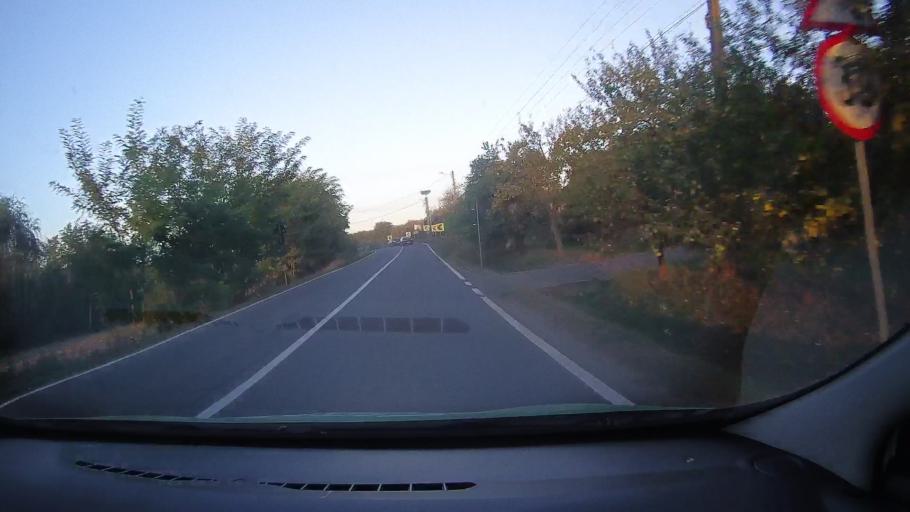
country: RO
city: Szekelyhid
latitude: 47.3310
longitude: 22.0840
